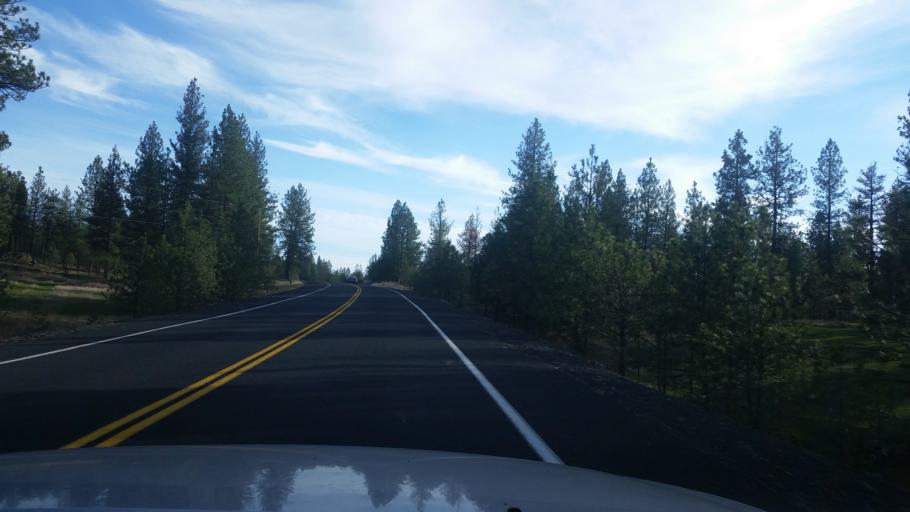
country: US
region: Washington
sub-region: Spokane County
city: Cheney
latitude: 47.3626
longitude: -117.5902
